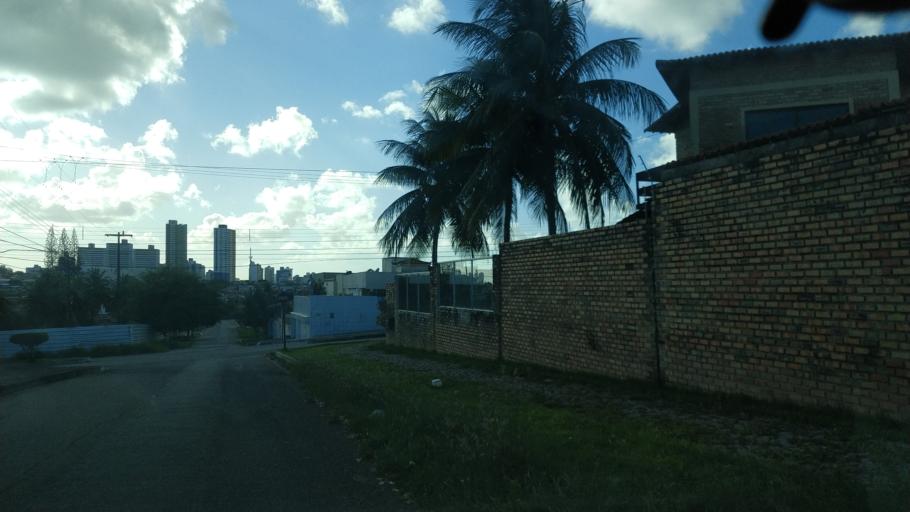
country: BR
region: Rio Grande do Norte
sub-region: Natal
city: Natal
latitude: -5.8469
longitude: -35.2054
